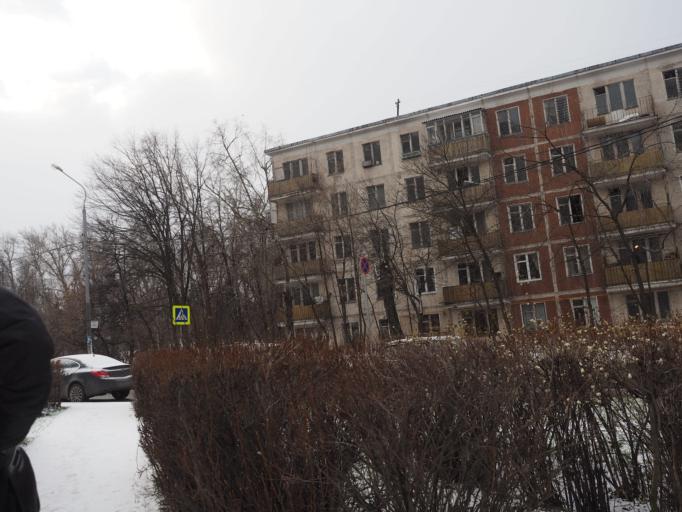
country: RU
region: Moscow
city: Davydkovo
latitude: 55.7309
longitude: 37.4599
